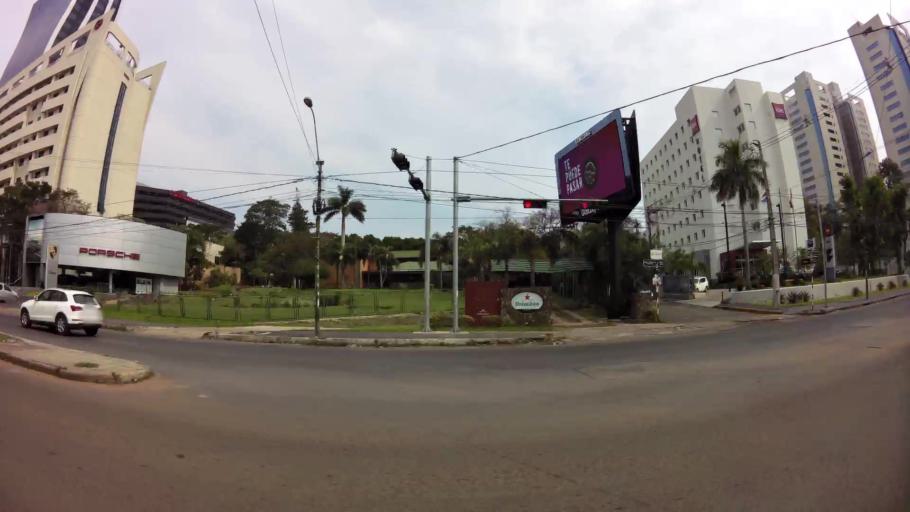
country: PY
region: Central
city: Fernando de la Mora
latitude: -25.2836
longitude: -57.5655
